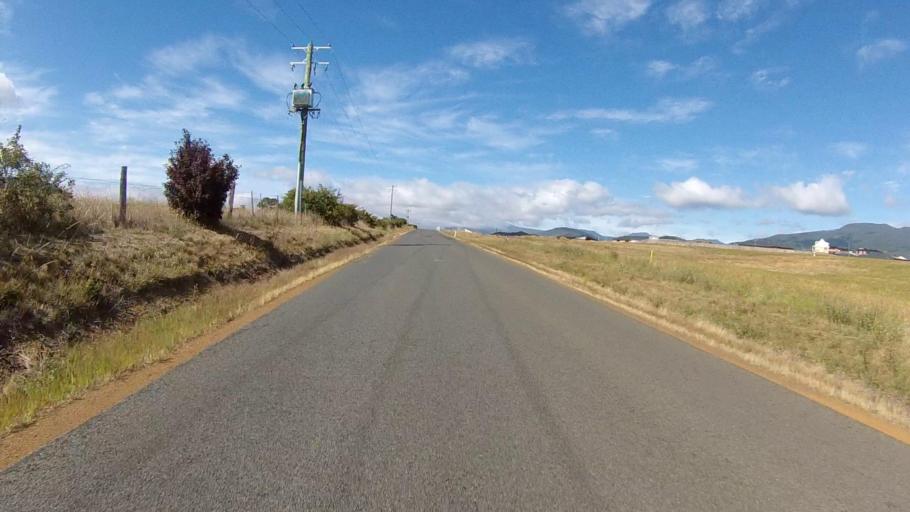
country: AU
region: Tasmania
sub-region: Brighton
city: Old Beach
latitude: -42.7599
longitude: 147.2796
